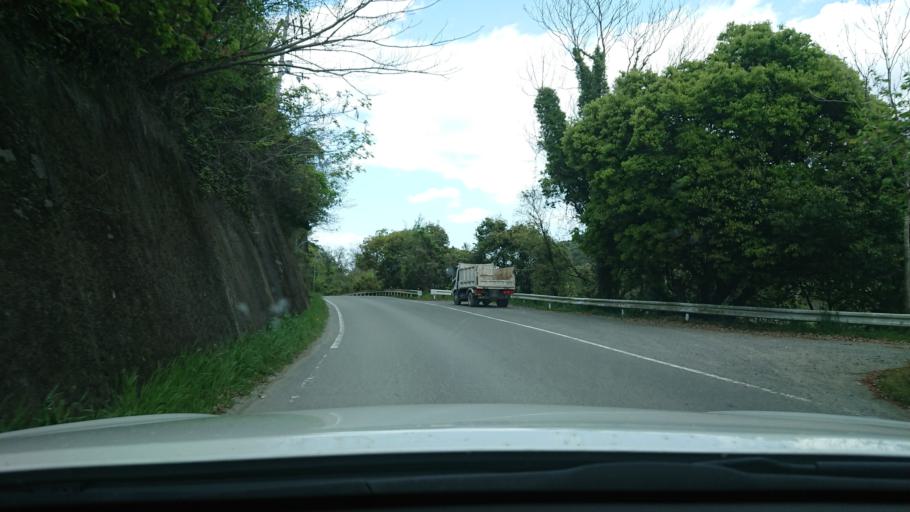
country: JP
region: Tokushima
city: Komatsushimacho
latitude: 33.9837
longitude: 134.5439
